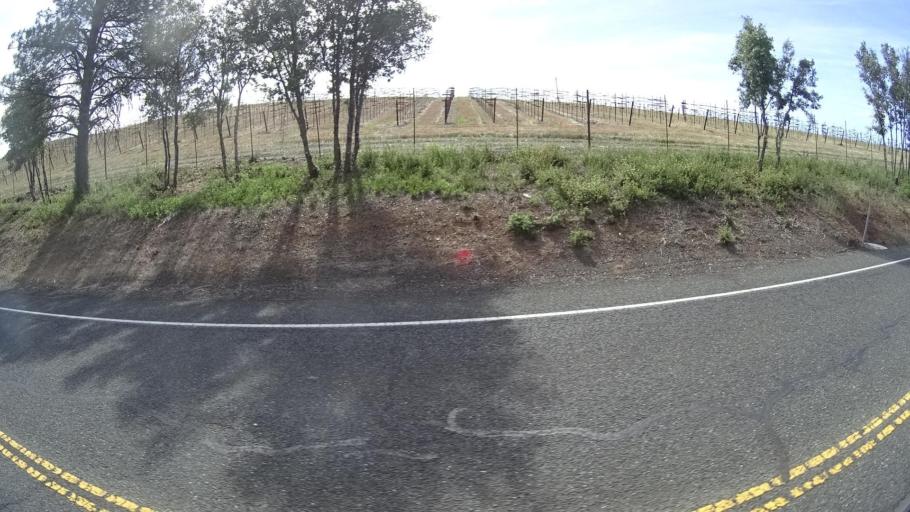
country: US
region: California
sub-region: Lake County
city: Soda Bay
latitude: 38.9368
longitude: -122.7398
